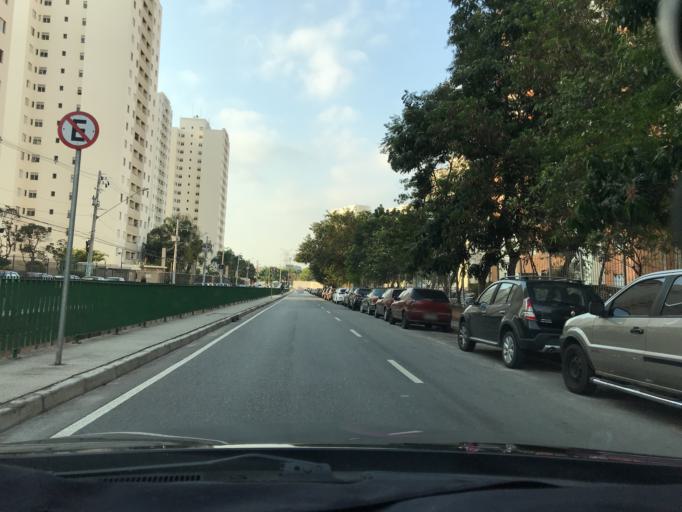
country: BR
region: Sao Paulo
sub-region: Osasco
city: Osasco
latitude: -23.5346
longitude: -46.7607
